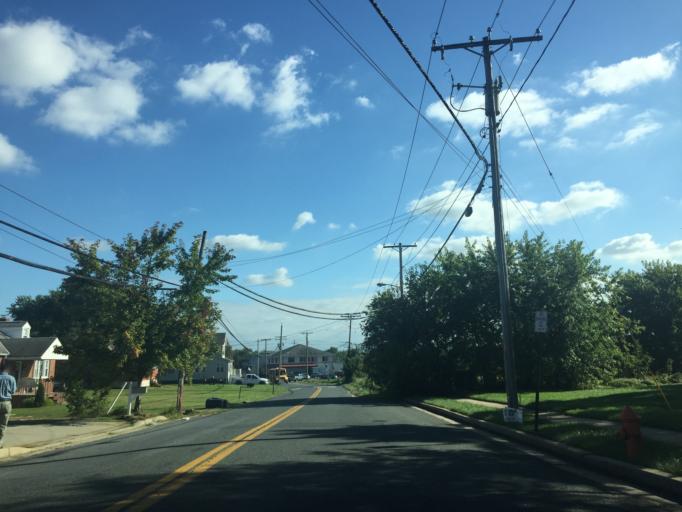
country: US
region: Maryland
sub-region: Baltimore County
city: Rossville
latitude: 39.3429
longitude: -76.4855
